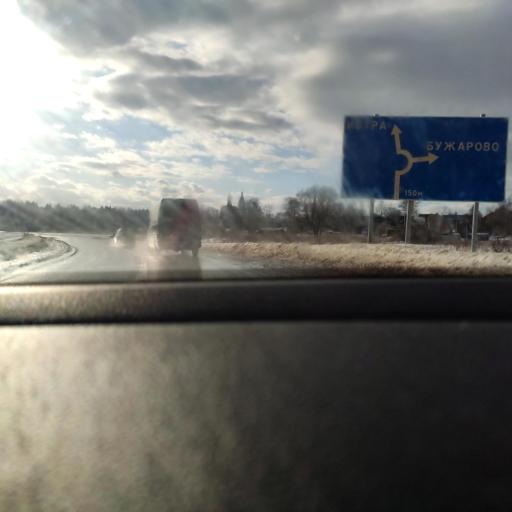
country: RU
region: Moskovskaya
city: Istra
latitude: 55.9821
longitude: 36.8132
